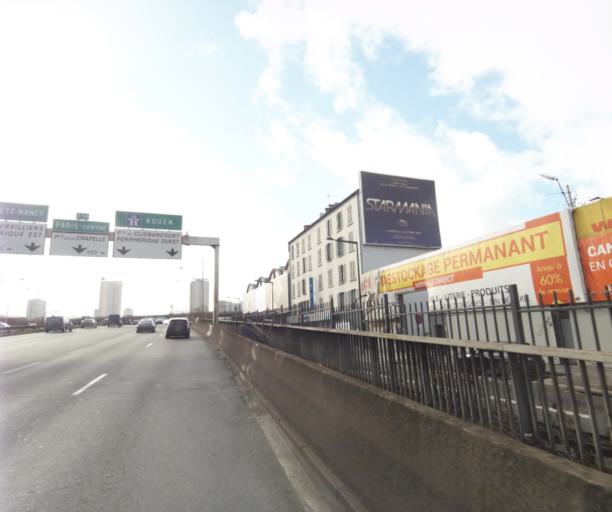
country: FR
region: Ile-de-France
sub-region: Paris
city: Saint-Ouen
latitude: 48.9033
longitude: 2.3585
